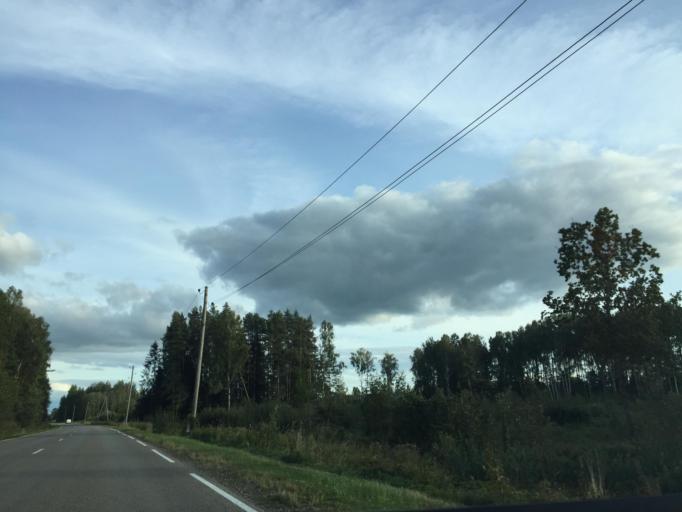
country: LV
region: Nereta
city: Nereta
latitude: 56.2983
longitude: 25.1103
